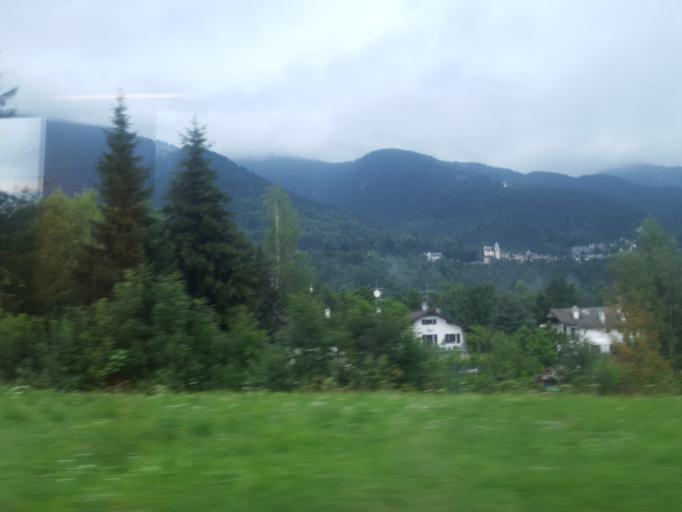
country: IT
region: Piedmont
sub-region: Provincia Verbano-Cusio-Ossola
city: Toceno
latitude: 46.1345
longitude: 8.4759
